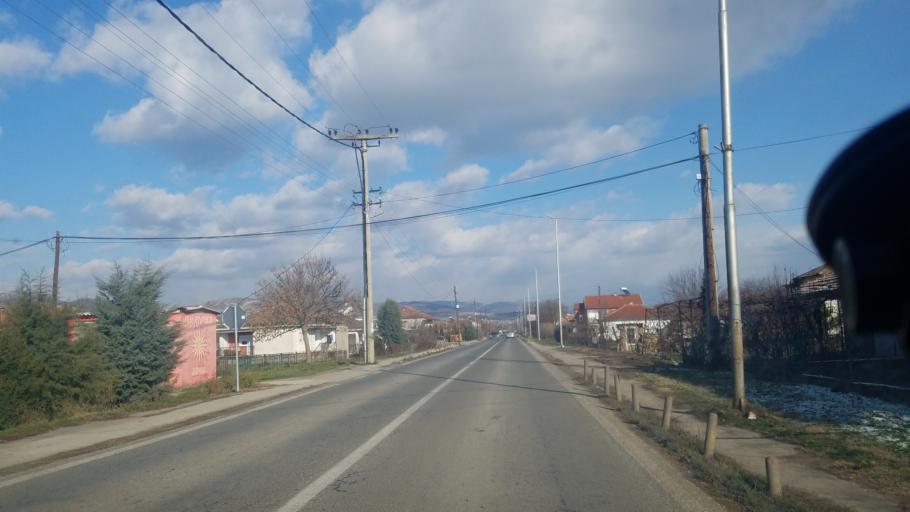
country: MK
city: Obleshevo
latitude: 41.8848
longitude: 22.3368
